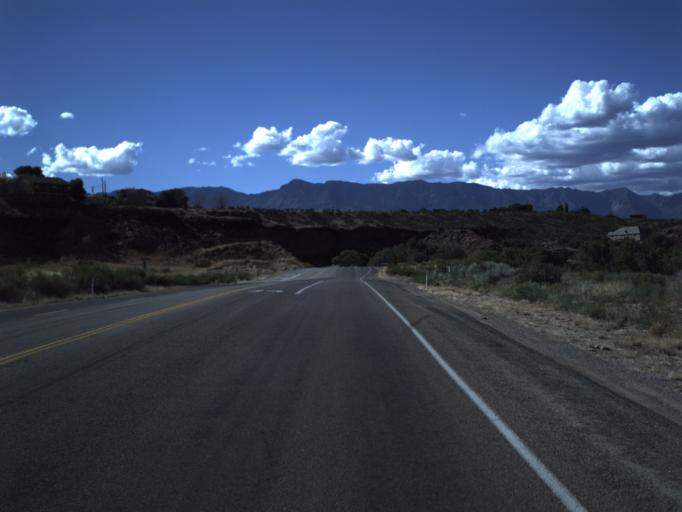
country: US
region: Utah
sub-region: Washington County
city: LaVerkin
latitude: 37.2212
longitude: -113.2777
